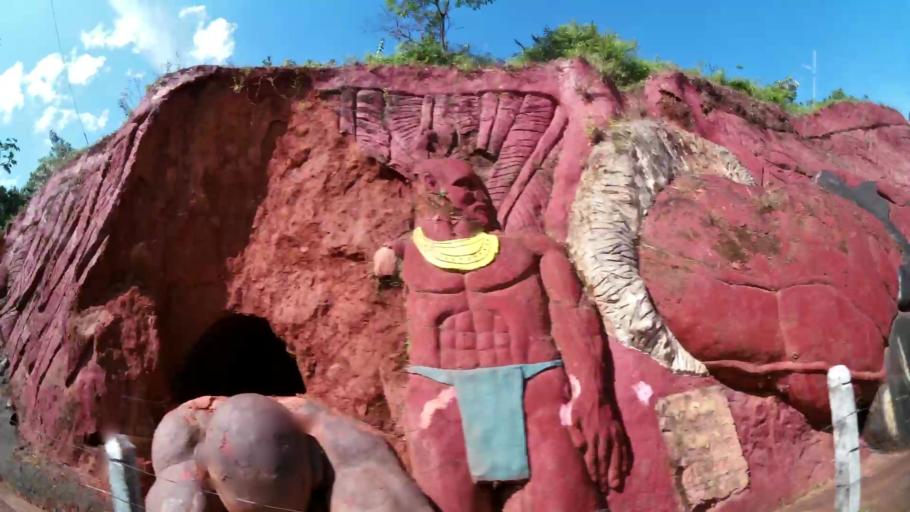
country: CO
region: Valle del Cauca
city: Cali
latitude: 3.4287
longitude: -76.5727
